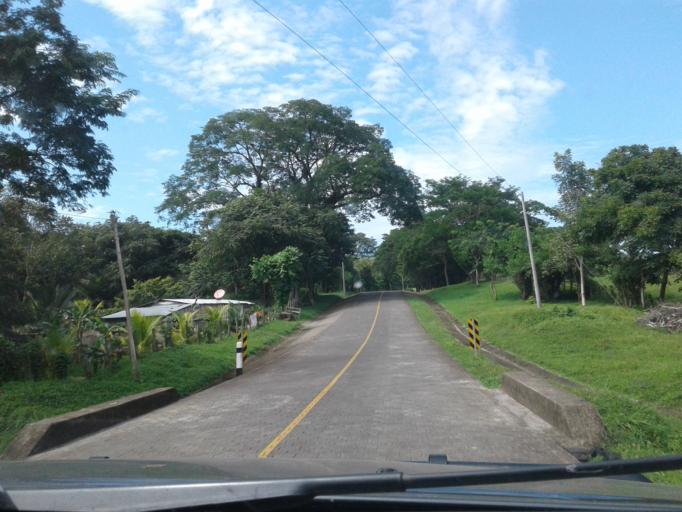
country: NI
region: Rivas
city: Cardenas
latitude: 11.1729
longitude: -85.4818
